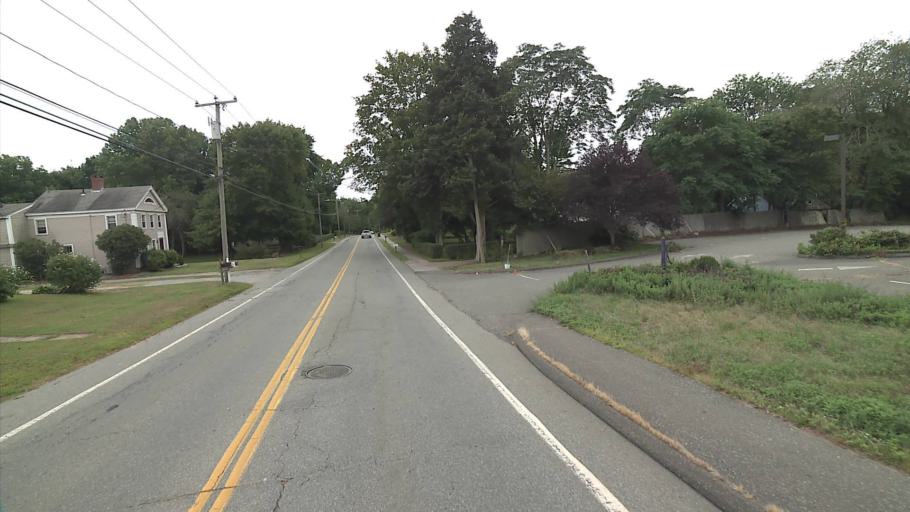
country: US
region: Connecticut
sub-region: New London County
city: Central Waterford
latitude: 41.3336
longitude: -72.1547
